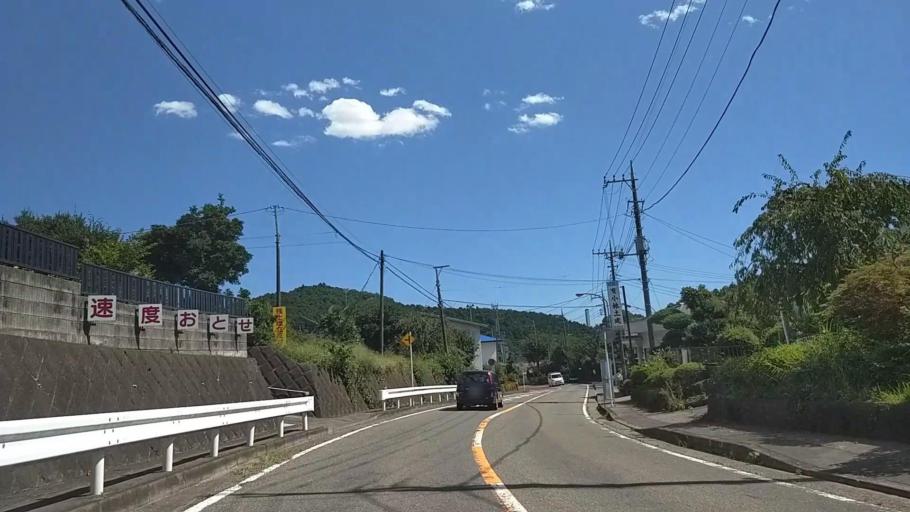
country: JP
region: Tokyo
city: Hachioji
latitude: 35.5495
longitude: 139.2945
